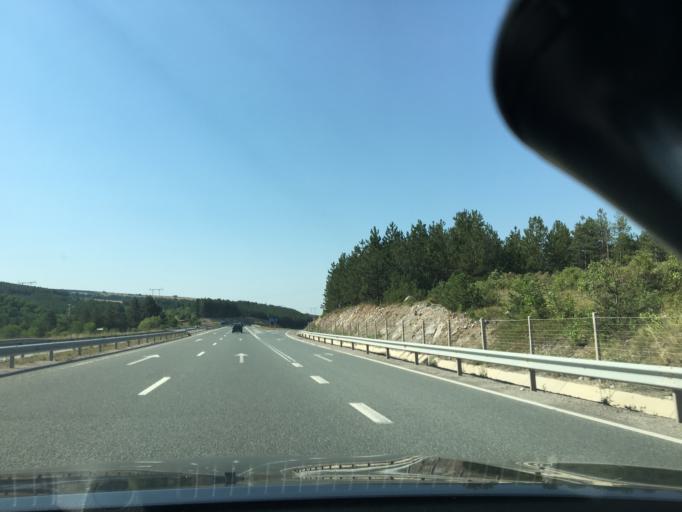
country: BG
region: Pernik
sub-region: Obshtina Pernik
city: Pernik
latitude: 42.5052
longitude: 23.1408
